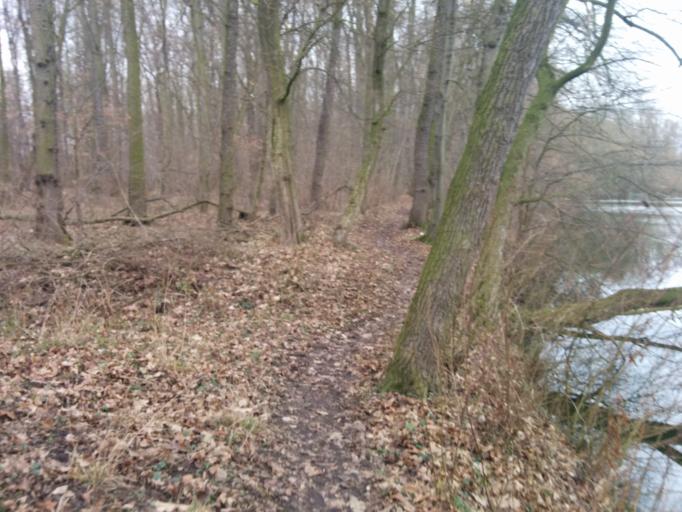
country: CZ
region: Central Bohemia
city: Libis
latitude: 50.2815
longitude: 14.5086
